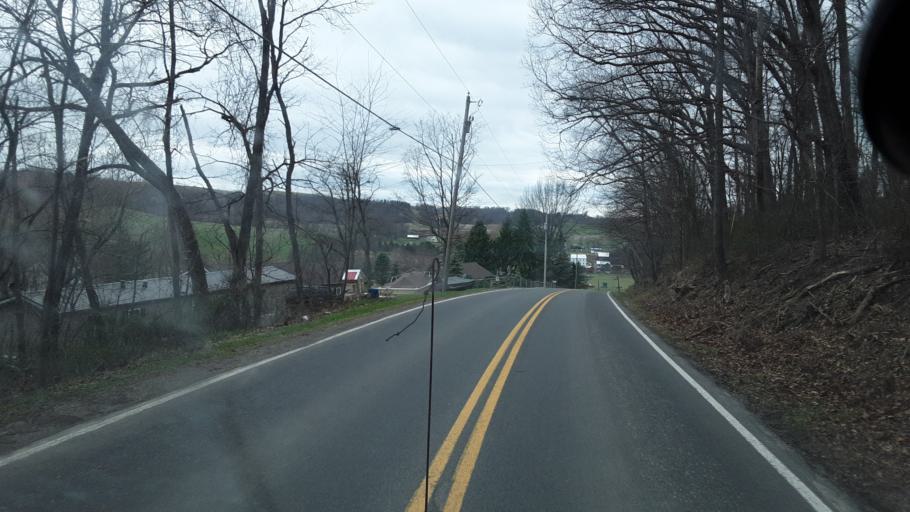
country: US
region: Ohio
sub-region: Stark County
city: Brewster
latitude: 40.7011
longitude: -81.6345
